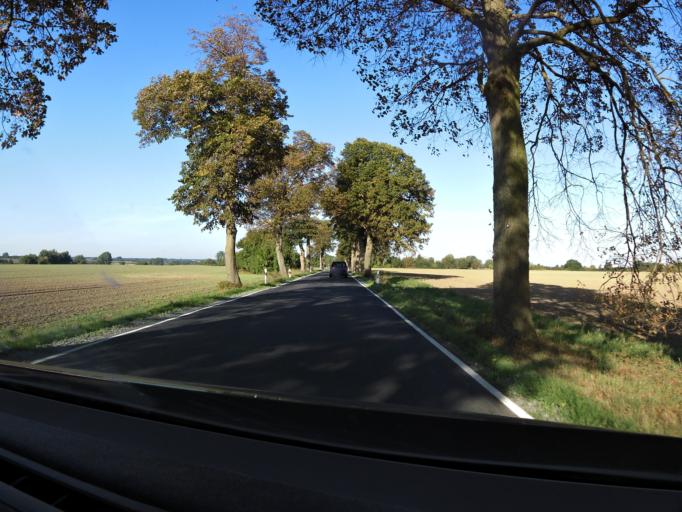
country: DE
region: Mecklenburg-Vorpommern
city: Kessin
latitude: 53.7925
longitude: 13.3514
